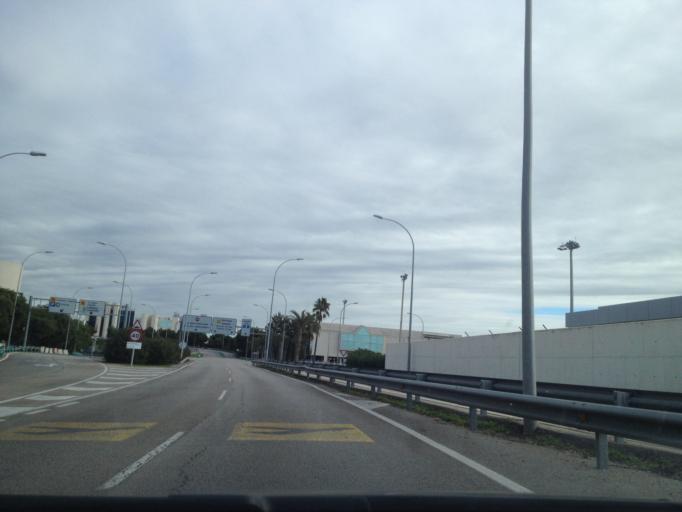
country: ES
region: Balearic Islands
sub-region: Illes Balears
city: s'Arenal
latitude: 39.5442
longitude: 2.7280
